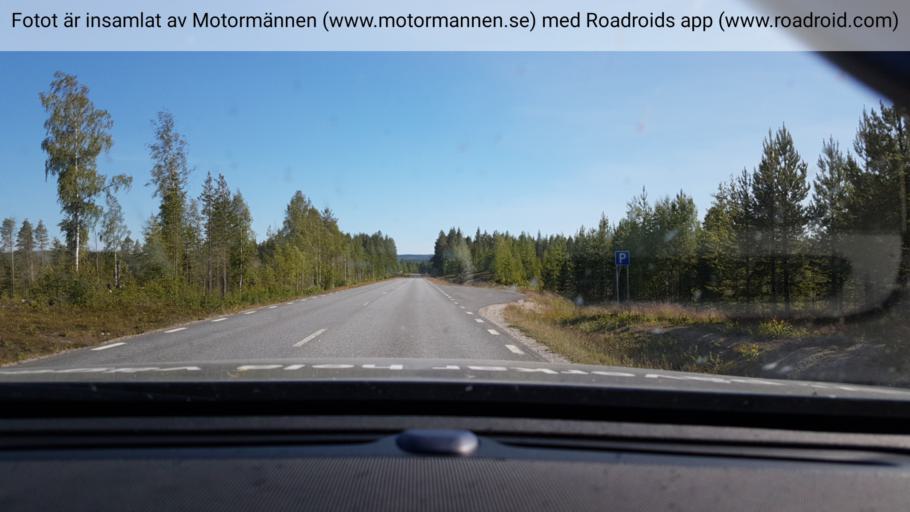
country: SE
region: Vaesterbotten
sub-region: Lycksele Kommun
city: Lycksele
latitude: 64.4966
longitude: 18.8977
